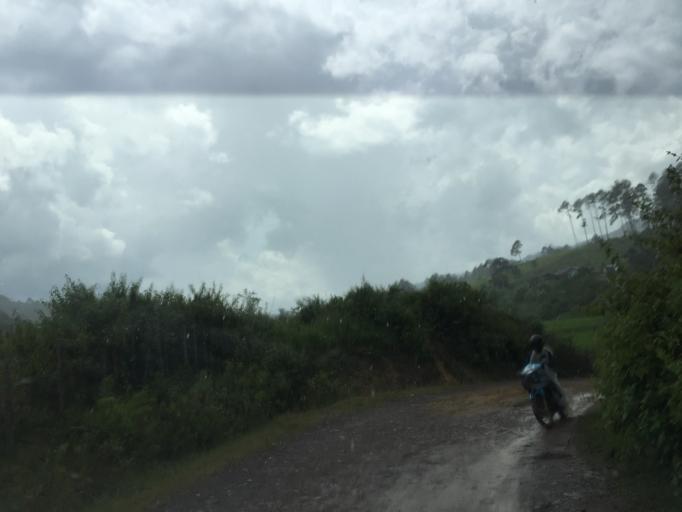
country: LA
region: Xiangkhoang
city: Muang Phonsavan
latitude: 19.3393
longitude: 103.5782
